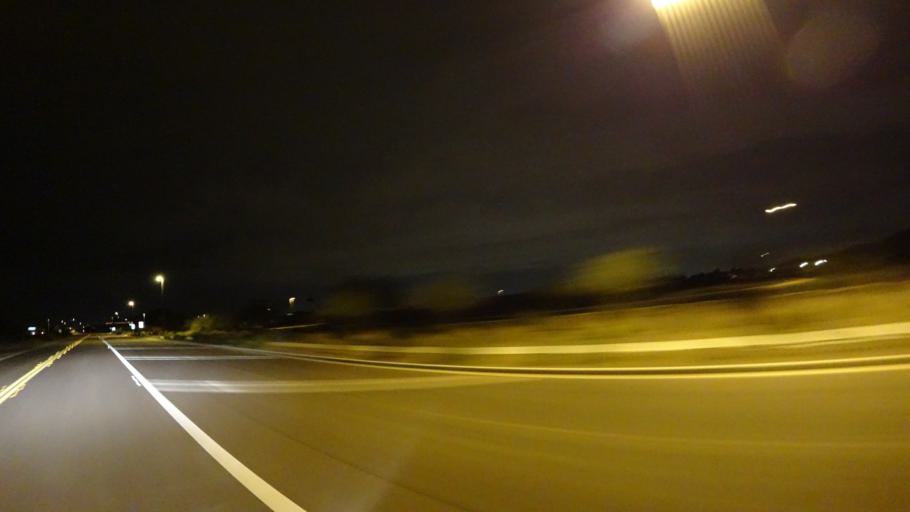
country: US
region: Arizona
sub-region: Pinal County
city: Apache Junction
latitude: 33.4326
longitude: -111.5980
